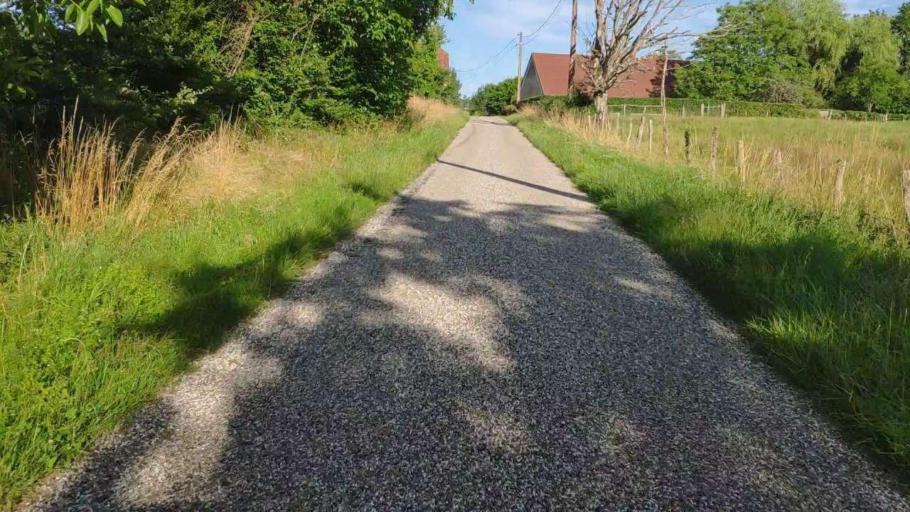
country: FR
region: Franche-Comte
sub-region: Departement du Jura
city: Bletterans
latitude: 46.7952
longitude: 5.4865
